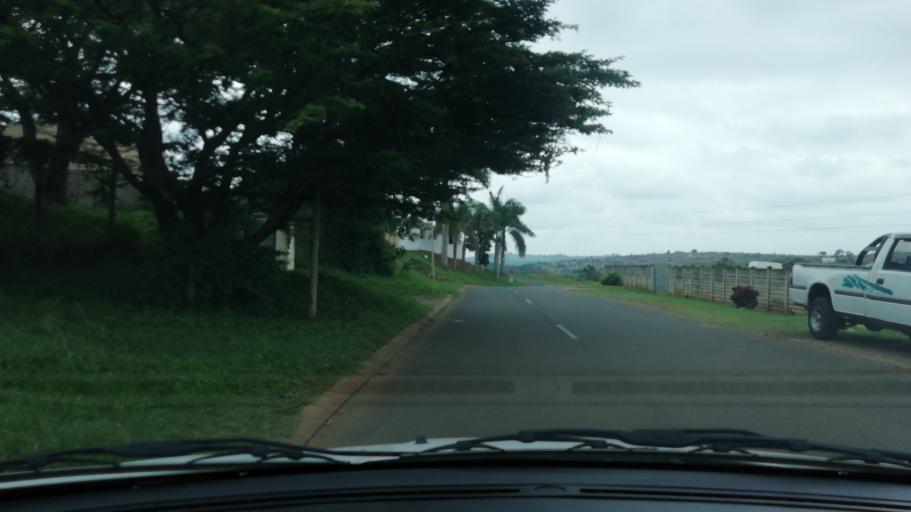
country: ZA
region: KwaZulu-Natal
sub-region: uThungulu District Municipality
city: Empangeni
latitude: -28.7611
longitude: 31.8854
